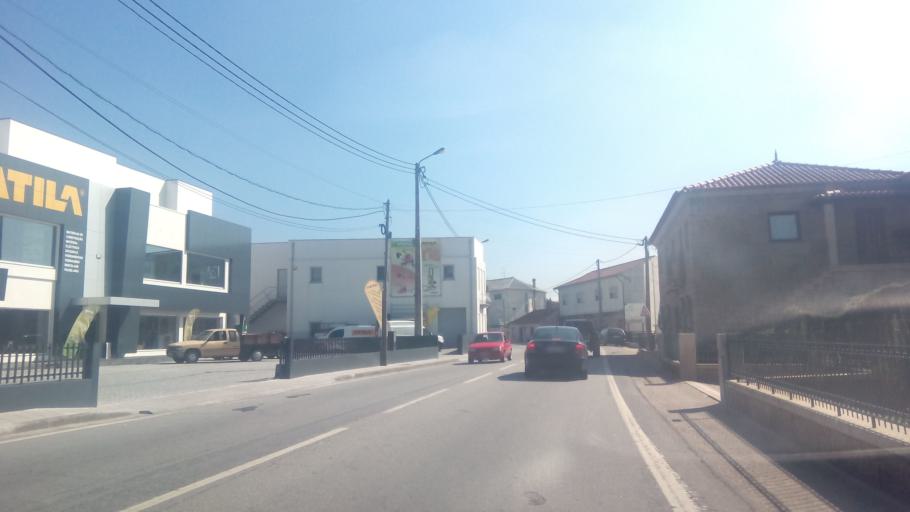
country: PT
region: Porto
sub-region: Paredes
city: Baltar
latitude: 41.1908
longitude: -8.3839
